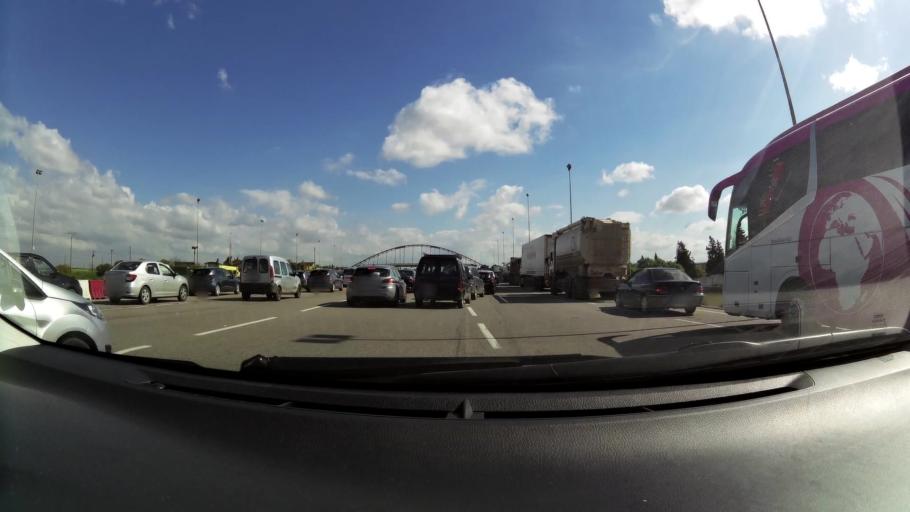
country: MA
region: Chaouia-Ouardigha
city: Nouaseur
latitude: 33.3708
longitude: -7.6211
